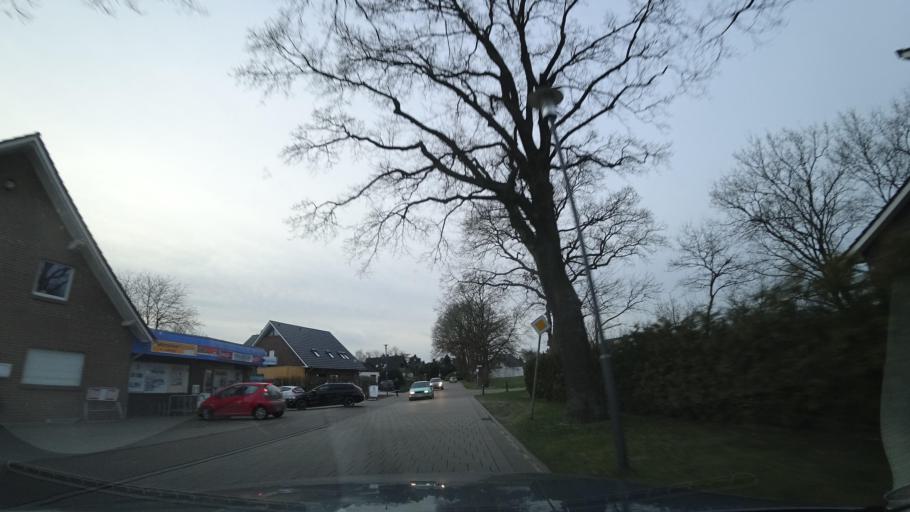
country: DE
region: Lower Saxony
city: Wardenburg
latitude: 53.0452
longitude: 8.2752
